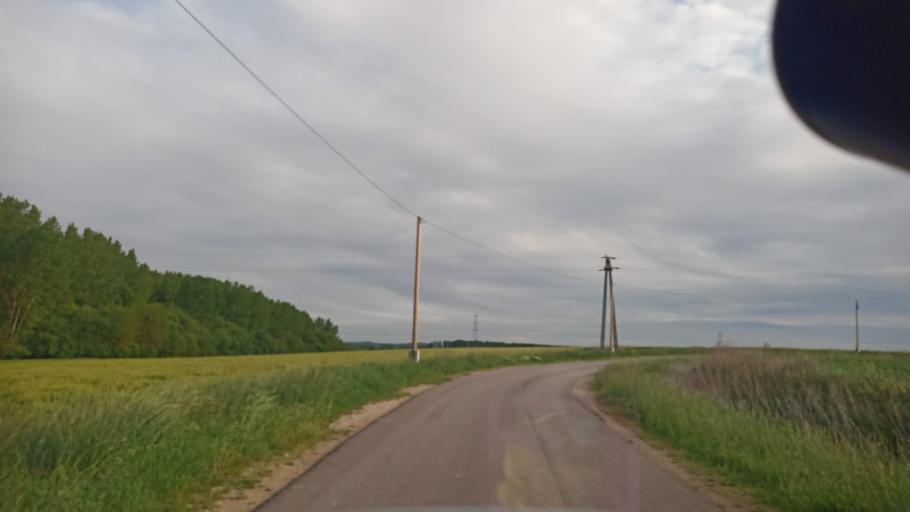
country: HU
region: Zala
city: Pacsa
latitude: 46.7513
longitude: 17.0209
